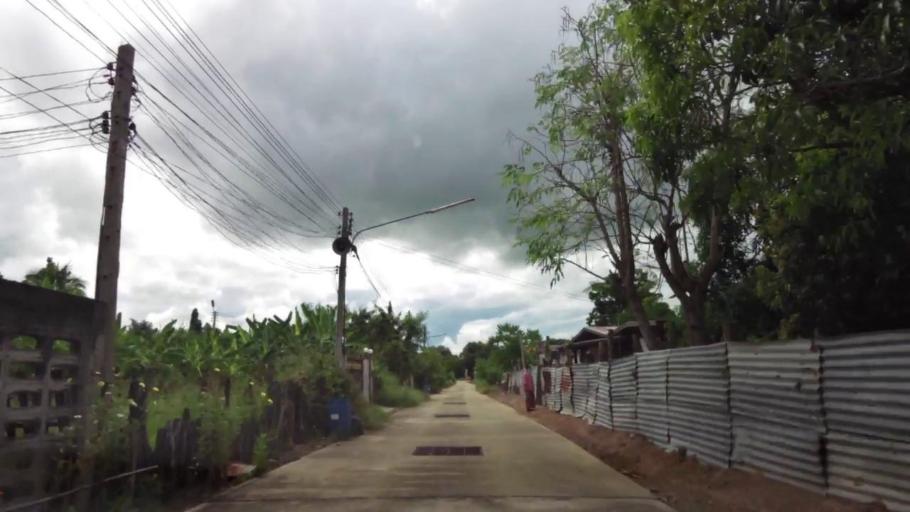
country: TH
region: Nakhon Sawan
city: Phai Sali
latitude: 15.6013
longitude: 100.6588
